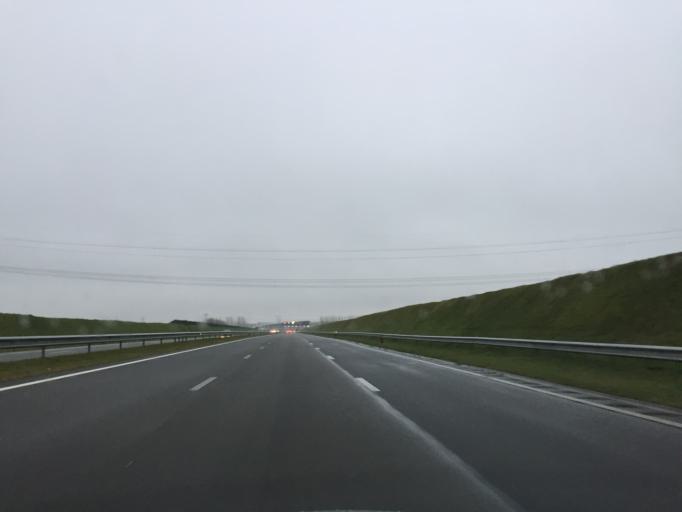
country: NL
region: Zeeland
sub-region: Gemeente Borsele
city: Borssele
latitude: 51.4352
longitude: 3.7590
